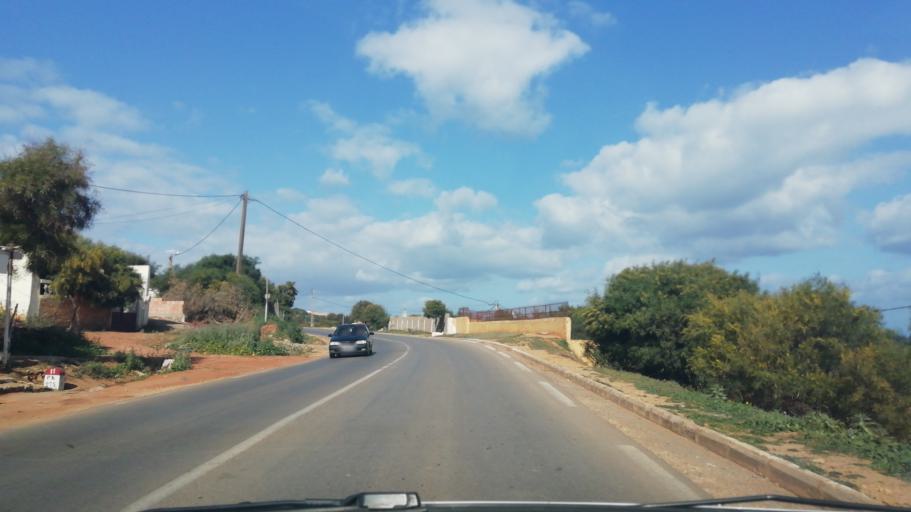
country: DZ
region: Relizane
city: Mazouna
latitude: 36.3266
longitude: 0.6943
